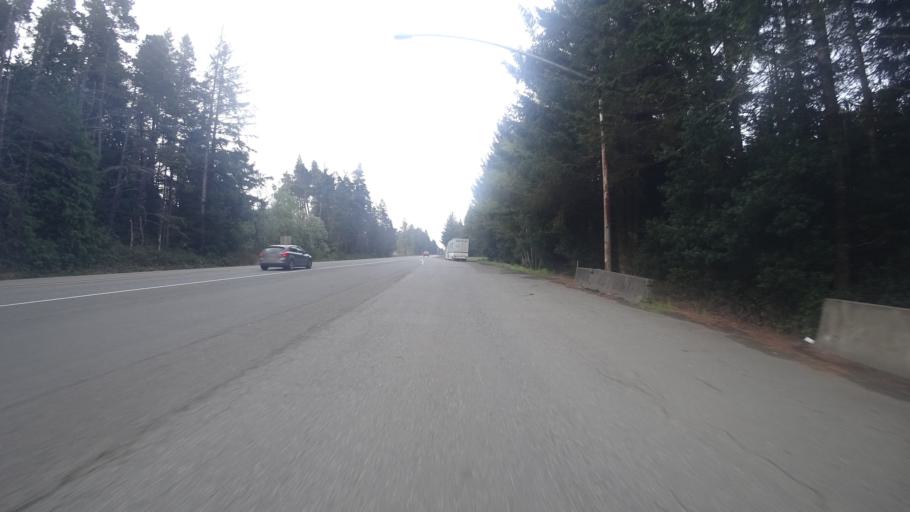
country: US
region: Oregon
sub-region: Coos County
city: Lakeside
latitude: 43.5123
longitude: -124.2175
